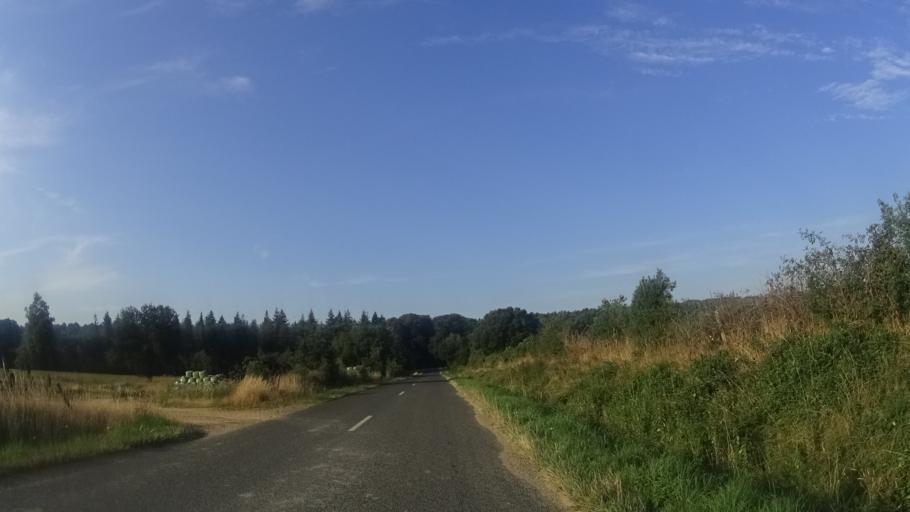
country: FR
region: Pays de la Loire
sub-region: Departement de la Loire-Atlantique
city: Saint-Mars-la-Jaille
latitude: 47.5513
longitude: -1.2287
